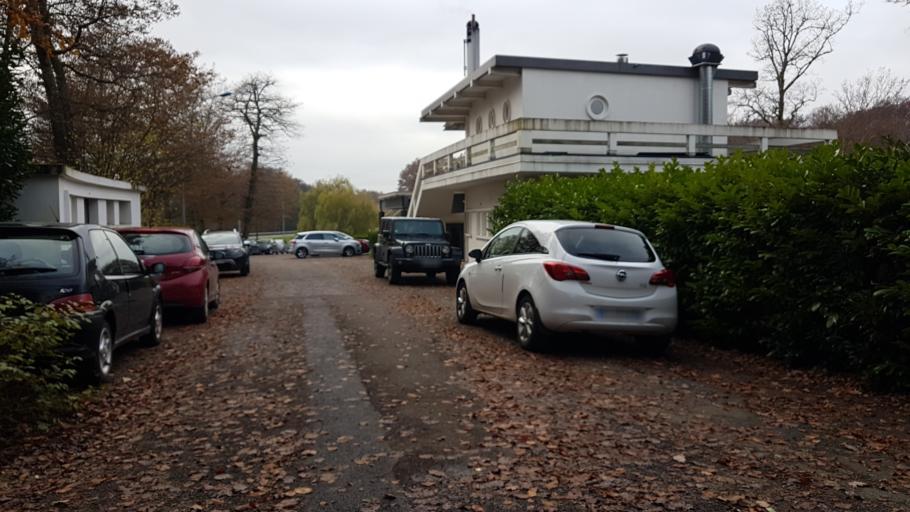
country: FR
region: Franche-Comte
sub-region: Departement de la Haute-Saone
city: Luxeuil-les-Bains
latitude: 47.8093
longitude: 6.3533
